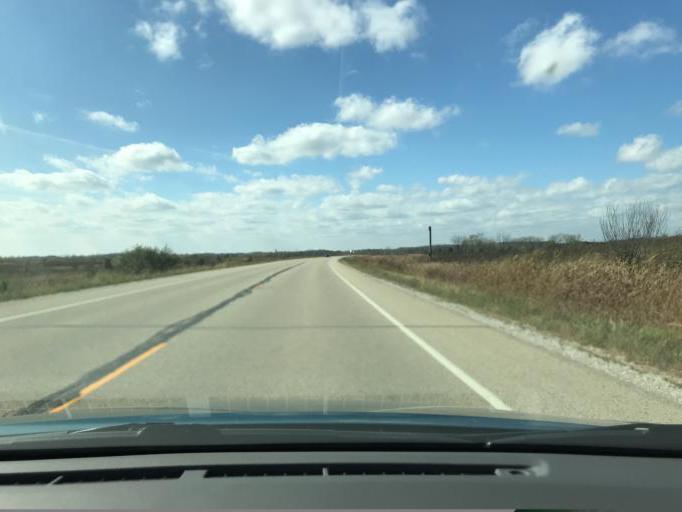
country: US
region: Wisconsin
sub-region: Kenosha County
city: Paddock Lake
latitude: 42.6357
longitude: -88.1315
